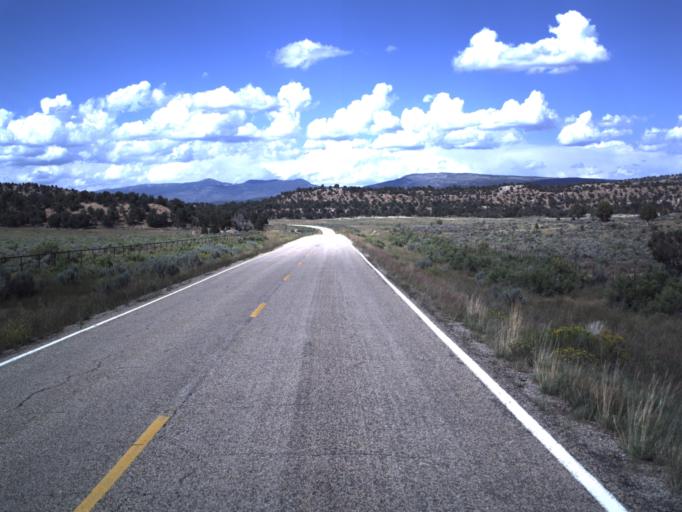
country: US
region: Utah
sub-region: Duchesne County
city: Duchesne
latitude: 40.2681
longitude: -110.7048
